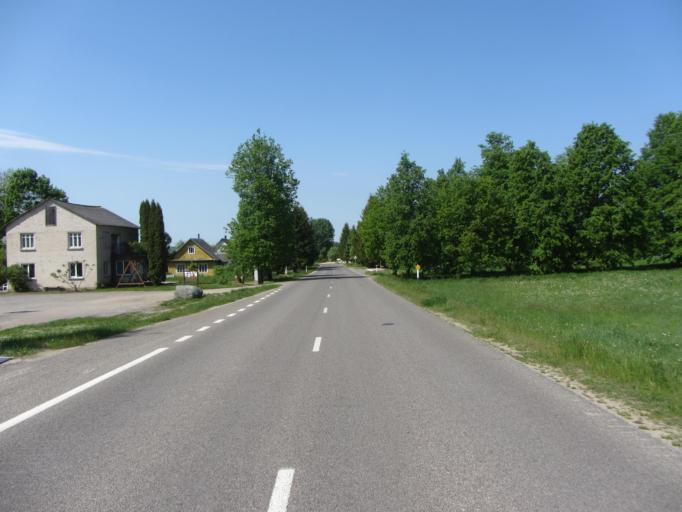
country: LT
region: Utenos apskritis
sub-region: Utena
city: Utena
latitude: 55.6122
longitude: 25.3982
